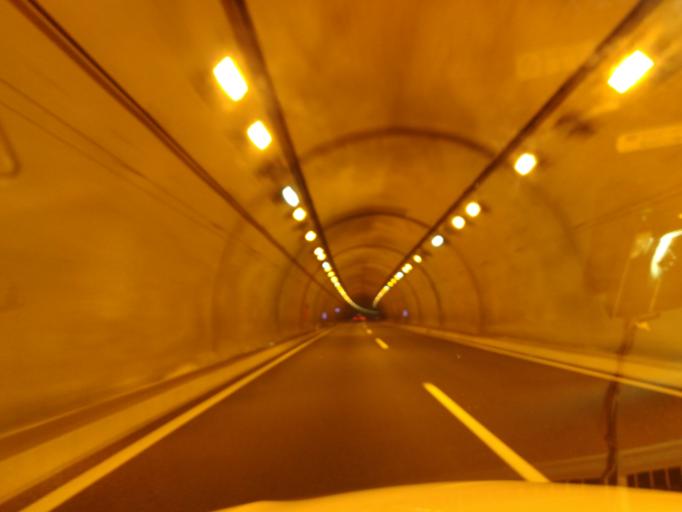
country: JP
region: Ehime
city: Kawanoecho
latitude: 33.8042
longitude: 133.6609
